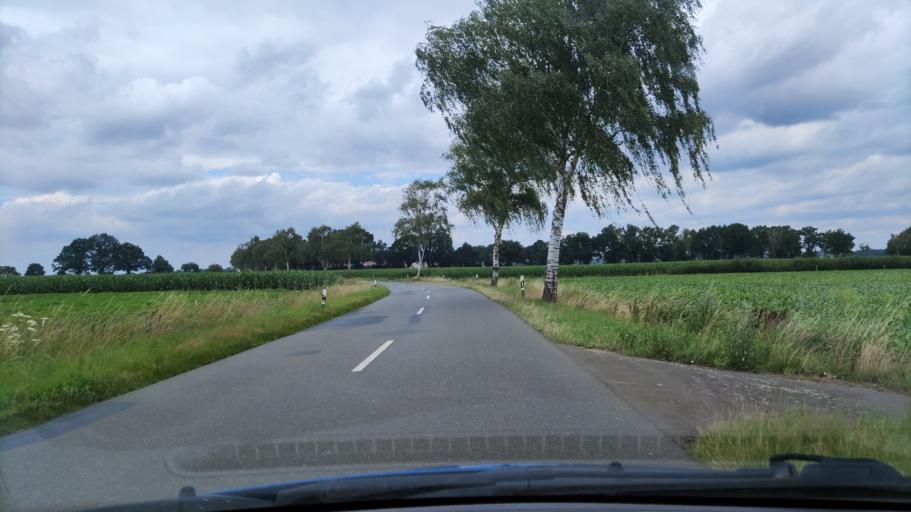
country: DE
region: Lower Saxony
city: Romstedt
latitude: 53.1287
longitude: 10.6391
